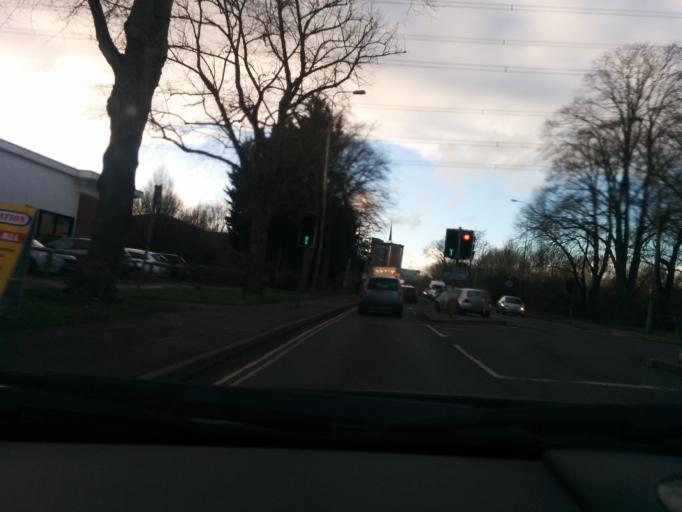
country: GB
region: England
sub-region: Oxfordshire
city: Oxford
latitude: 51.7531
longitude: -1.2891
